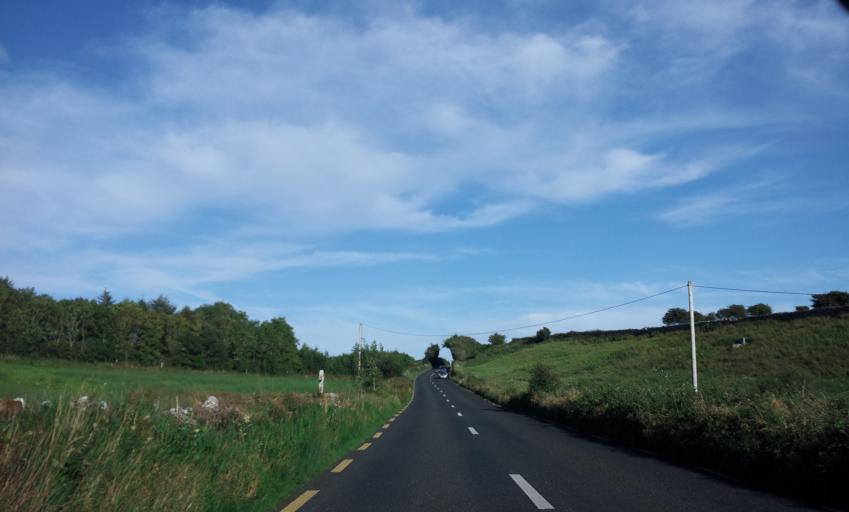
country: IE
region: Munster
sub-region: An Clar
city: Ennis
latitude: 52.9842
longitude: -9.1320
